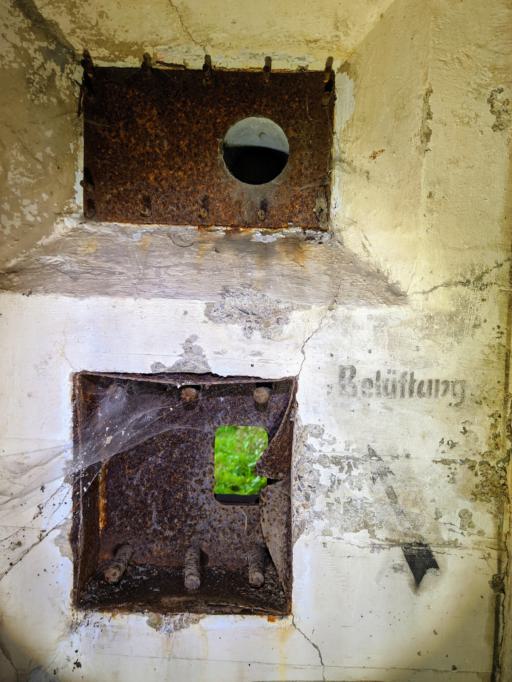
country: PL
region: Lubusz
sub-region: Powiat swiebodzinski
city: Lubrza
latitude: 52.3556
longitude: 15.4509
